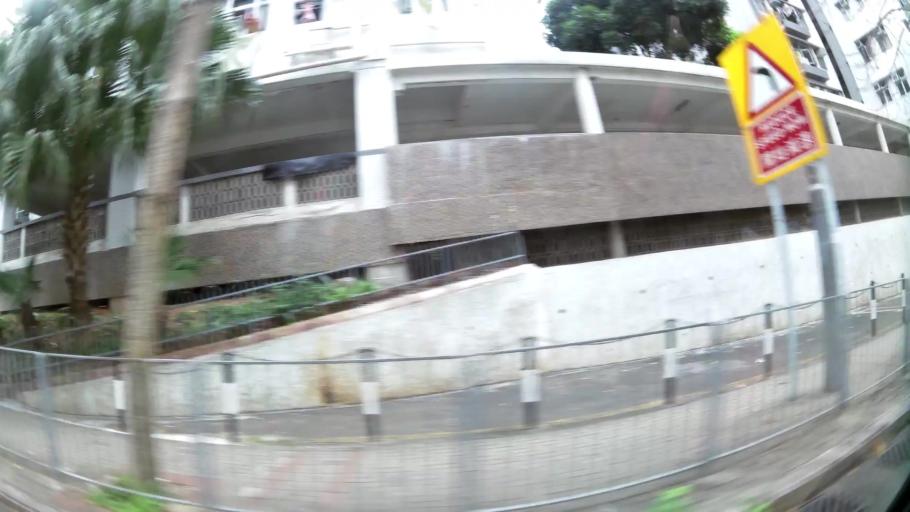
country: HK
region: Kowloon City
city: Kowloon
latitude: 22.3154
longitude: 114.1799
